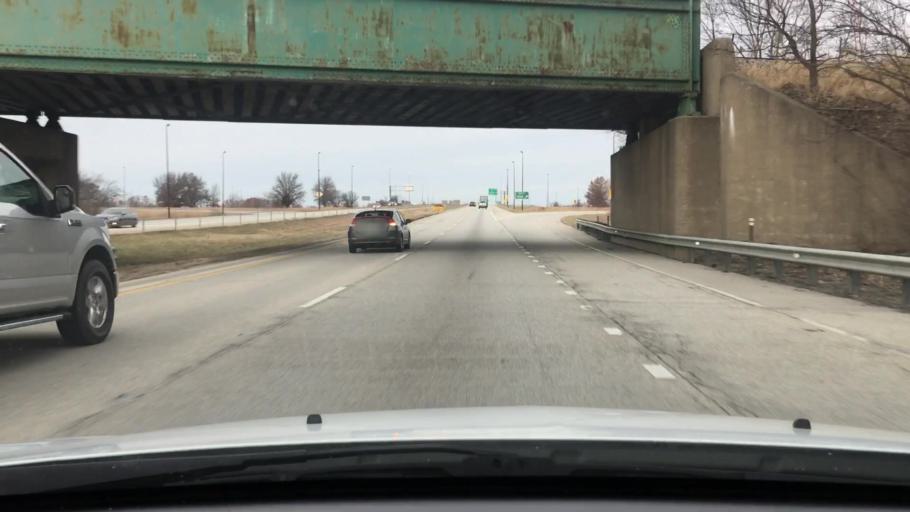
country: US
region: Illinois
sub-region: Sangamon County
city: Grandview
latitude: 39.8275
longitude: -89.5926
